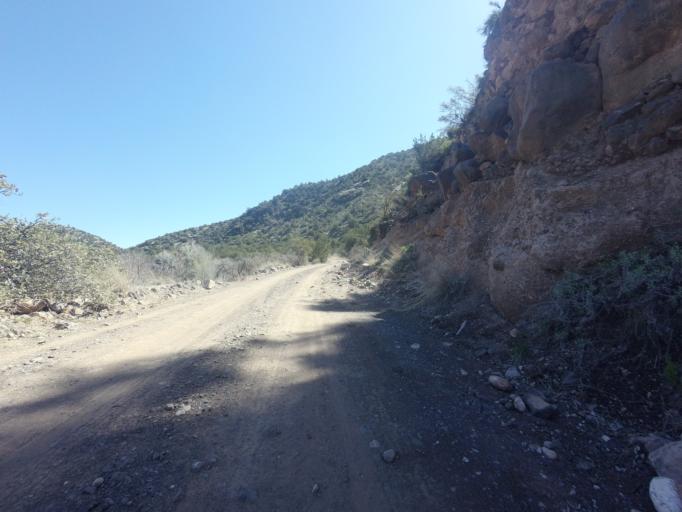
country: US
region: Arizona
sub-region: Gila County
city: Pine
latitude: 34.3968
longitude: -111.6281
